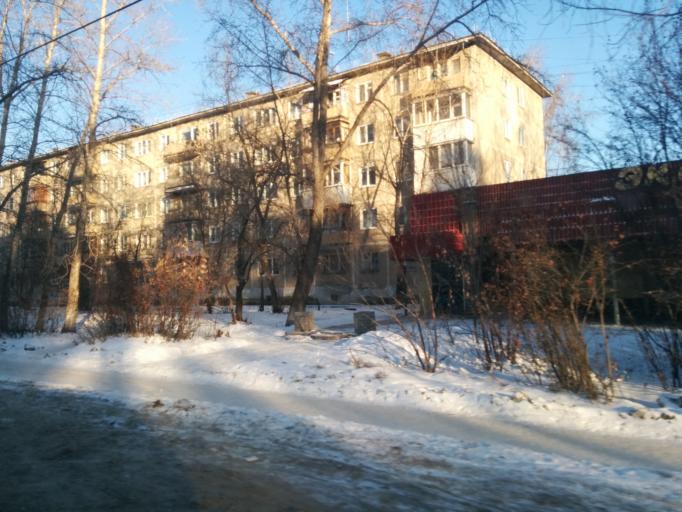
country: RU
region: Perm
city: Overyata
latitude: 58.0086
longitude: 55.9315
